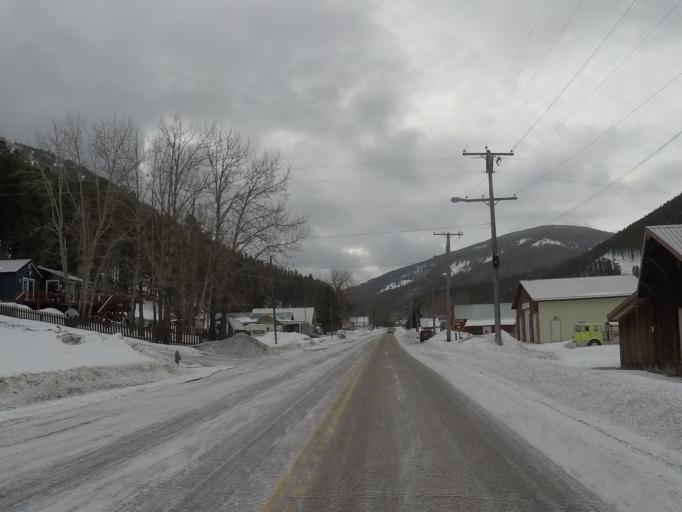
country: US
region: Montana
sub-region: Meagher County
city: White Sulphur Springs
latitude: 46.9335
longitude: -110.7358
